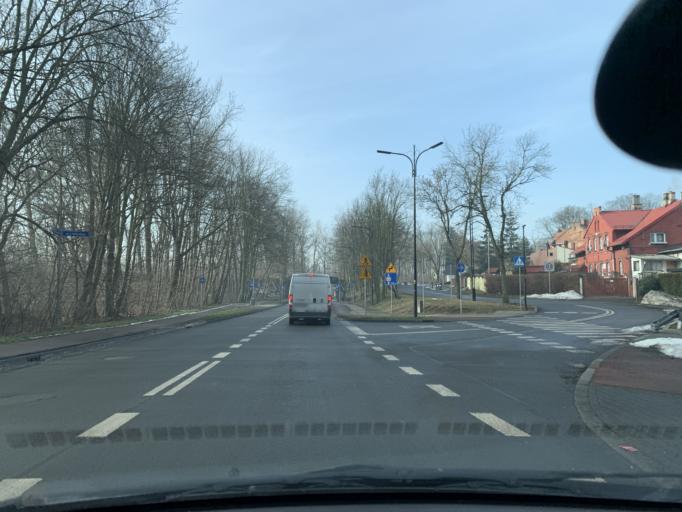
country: PL
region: Silesian Voivodeship
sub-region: Swietochlowice
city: Swietochlowice
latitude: 50.3272
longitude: 18.8617
